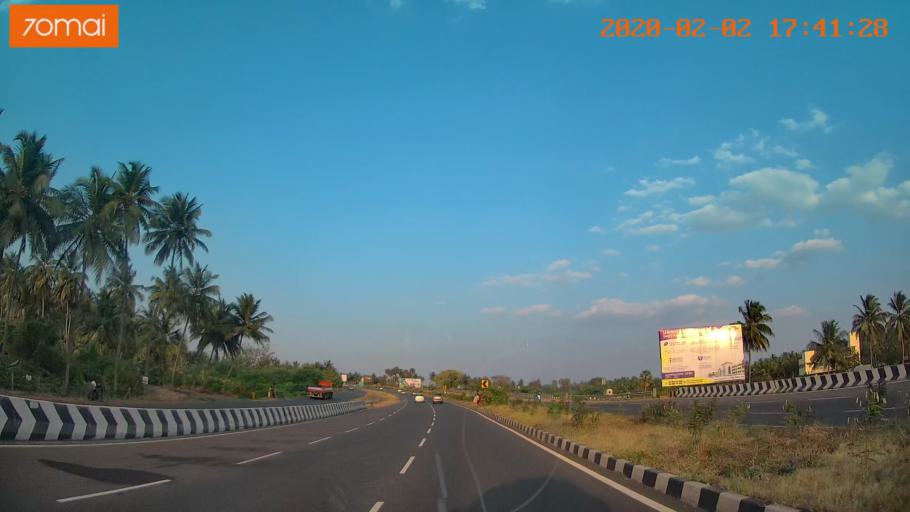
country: IN
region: Tamil Nadu
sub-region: Coimbatore
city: Madukkarai
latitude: 10.8743
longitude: 76.9019
